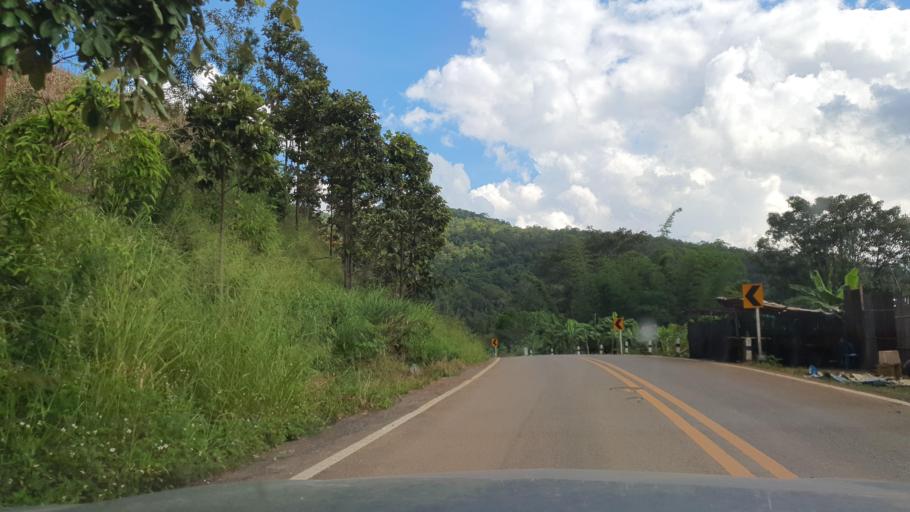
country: TH
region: Chiang Rai
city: Wiang Pa Pao
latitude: 19.3099
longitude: 99.4159
